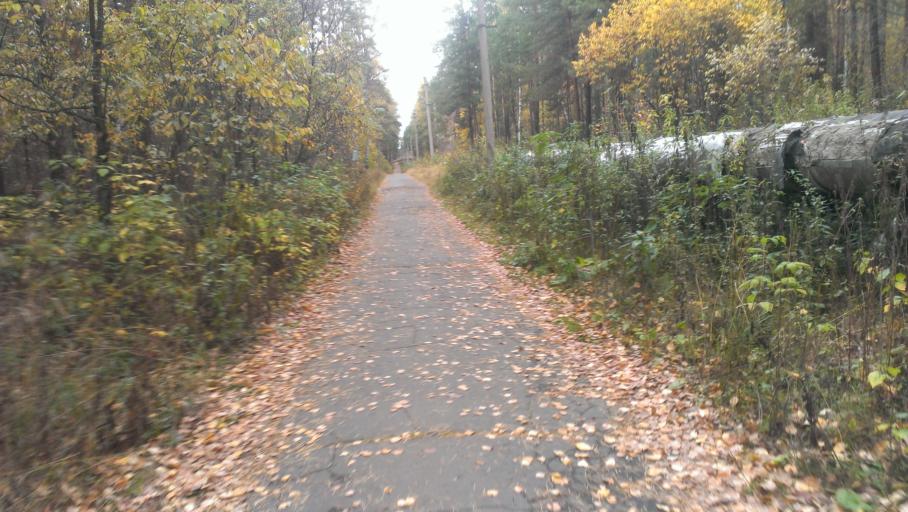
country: RU
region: Altai Krai
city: Yuzhnyy
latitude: 53.2619
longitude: 83.6873
